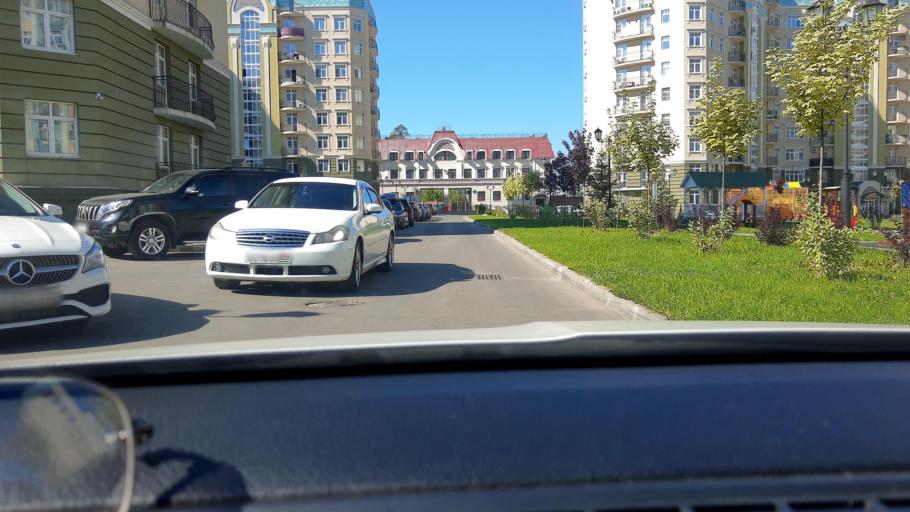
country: RU
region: Moskovskaya
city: Petrovo-Dal'neye
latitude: 55.7735
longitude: 37.2185
